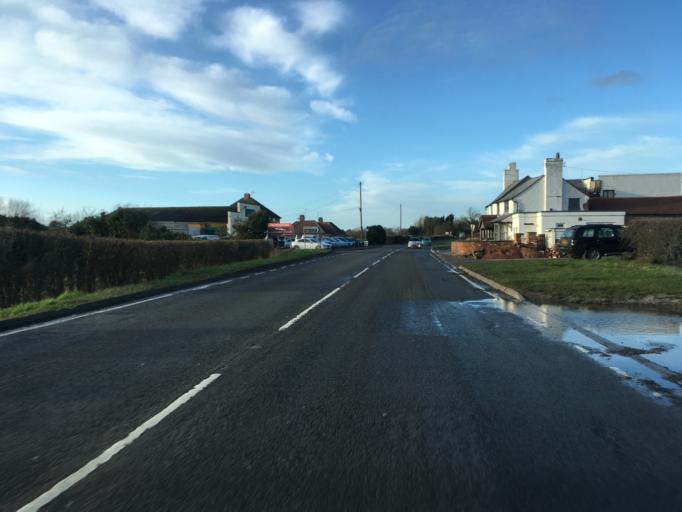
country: GB
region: England
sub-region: Warwickshire
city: Stratford-upon-Avon
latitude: 52.2226
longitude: -1.7352
